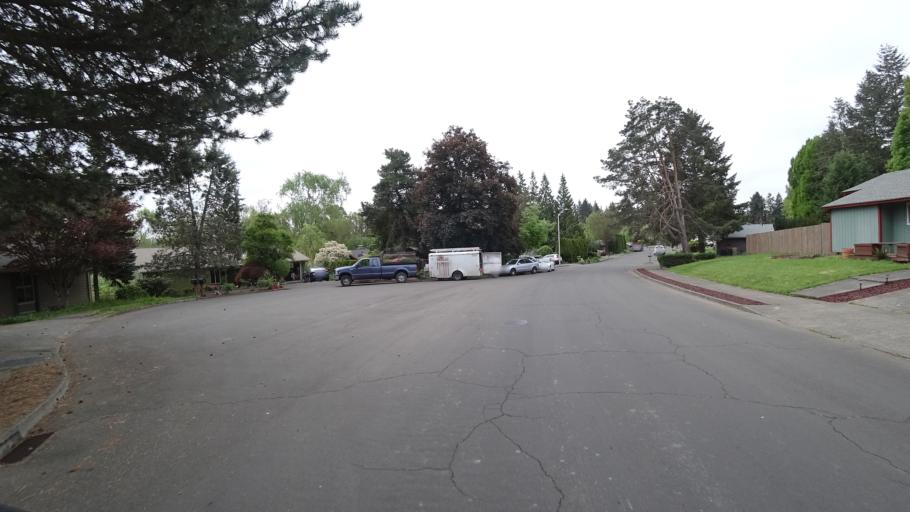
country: US
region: Oregon
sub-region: Washington County
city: Aloha
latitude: 45.5148
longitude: -122.8705
